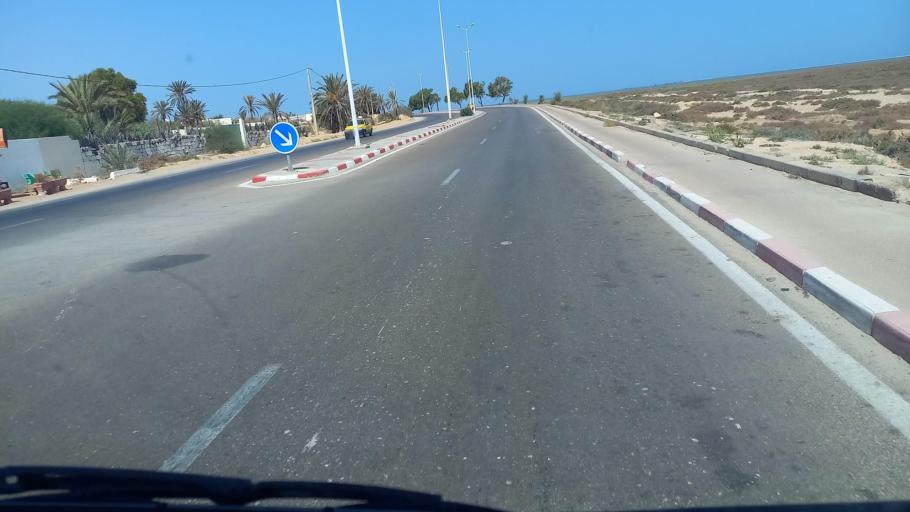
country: TN
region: Madanin
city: Houmt Souk
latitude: 33.8711
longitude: 10.9362
